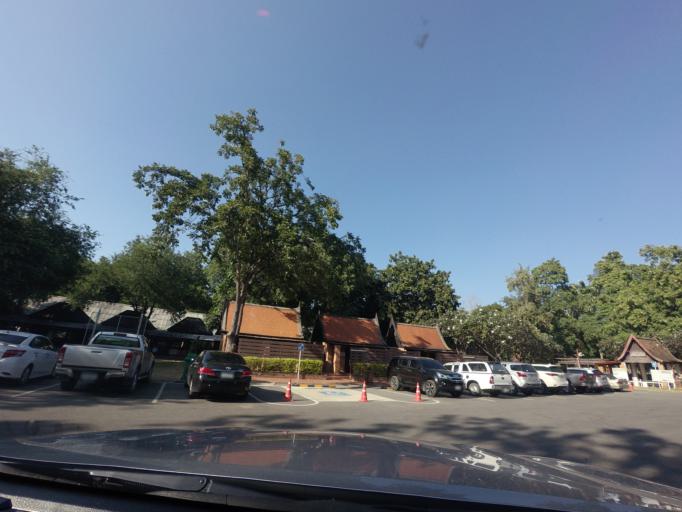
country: TH
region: Sukhothai
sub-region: Amphoe Si Satchanalai
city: Si Satchanalai
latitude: 17.4256
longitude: 99.7881
